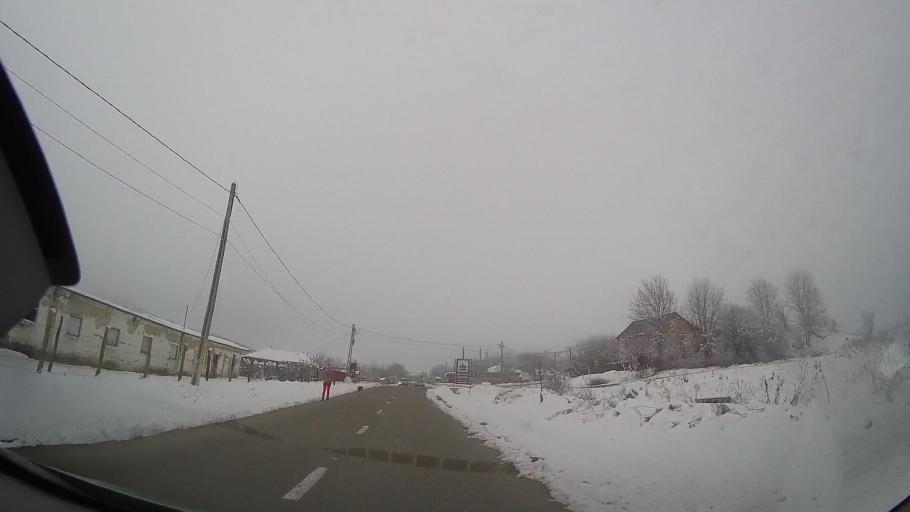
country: RO
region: Neamt
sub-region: Comuna Valea Ursului
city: Valea Ursului
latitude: 46.8006
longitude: 27.1166
